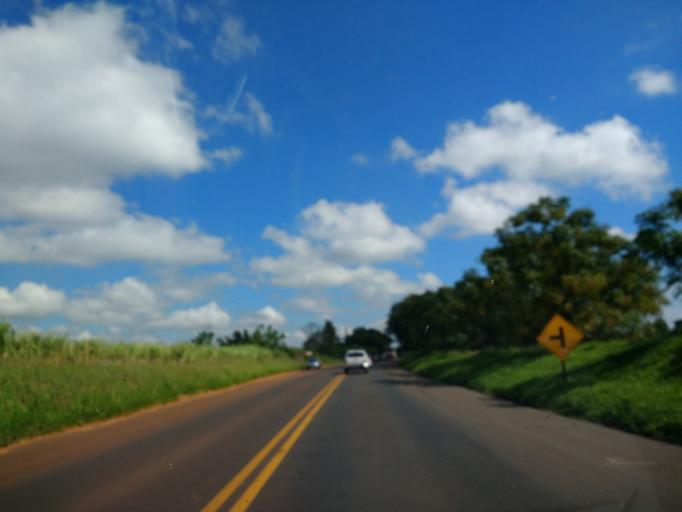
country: BR
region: Parana
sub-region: Umuarama
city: Umuarama
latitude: -23.8231
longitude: -53.3375
